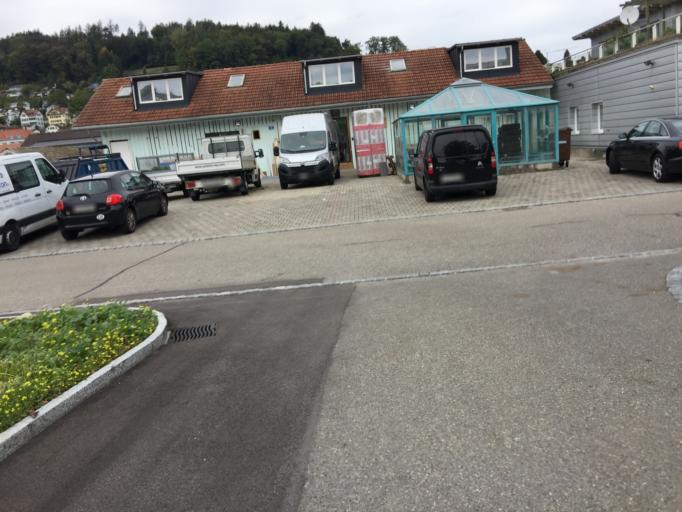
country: CH
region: Saint Gallen
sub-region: Wahlkreis Wil
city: Oberuzwil
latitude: 47.4313
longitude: 9.1300
